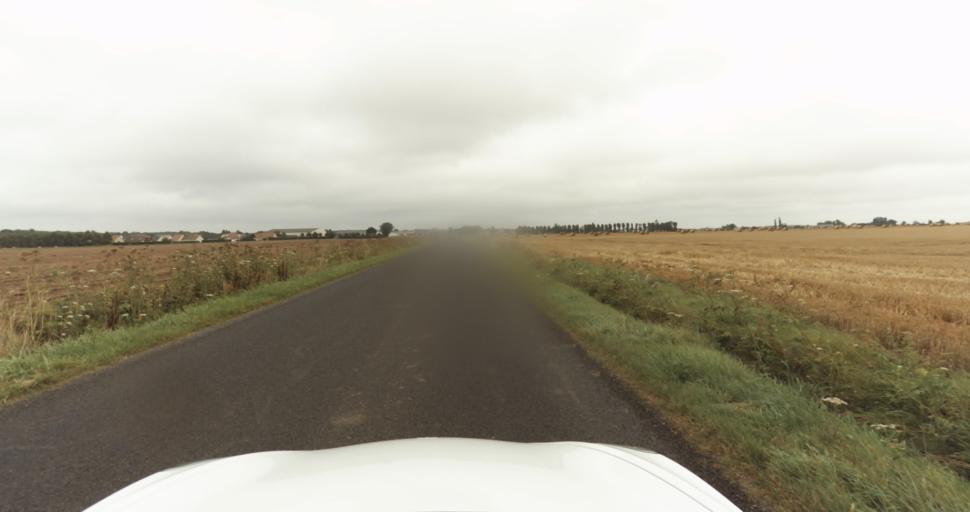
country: FR
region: Haute-Normandie
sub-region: Departement de l'Eure
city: Claville
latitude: 49.0879
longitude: 1.0637
